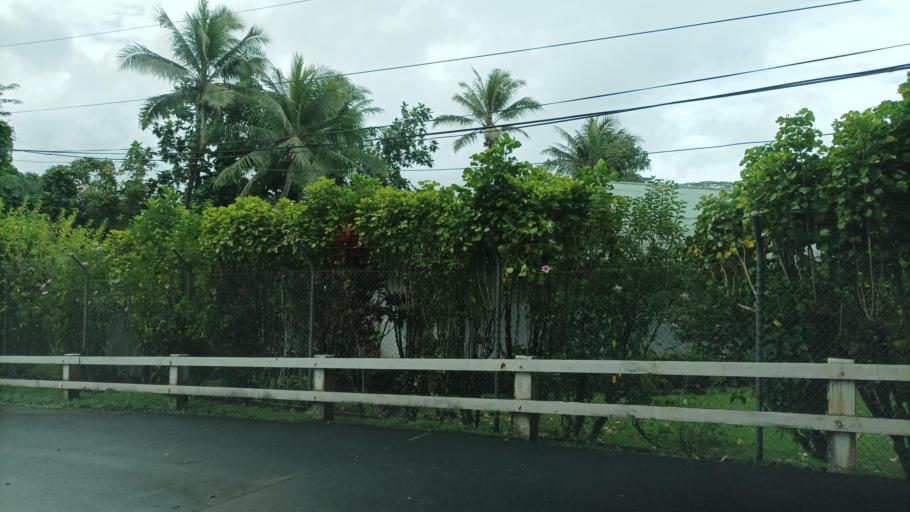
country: FM
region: Pohnpei
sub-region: Kolonia Municipality
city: Kolonia Town
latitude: 6.9517
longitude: 158.1980
